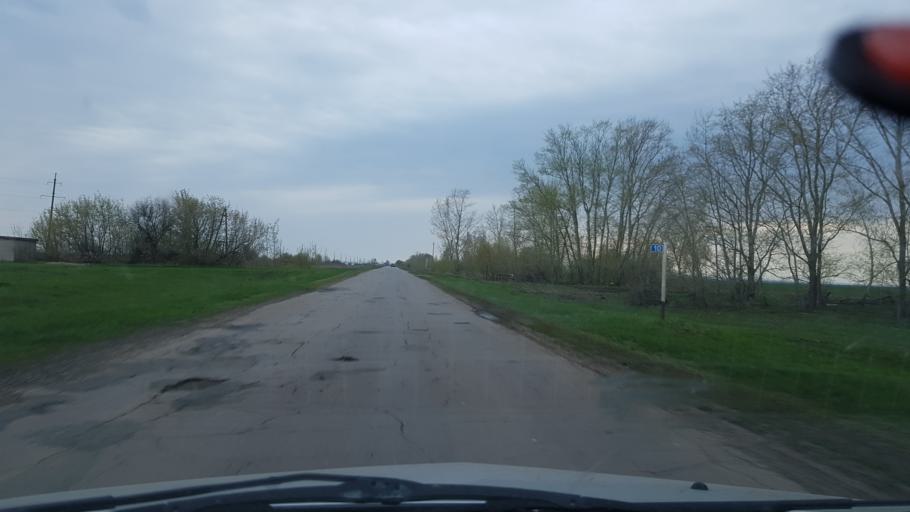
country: RU
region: Samara
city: Khryashchevka
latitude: 53.6684
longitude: 49.1384
